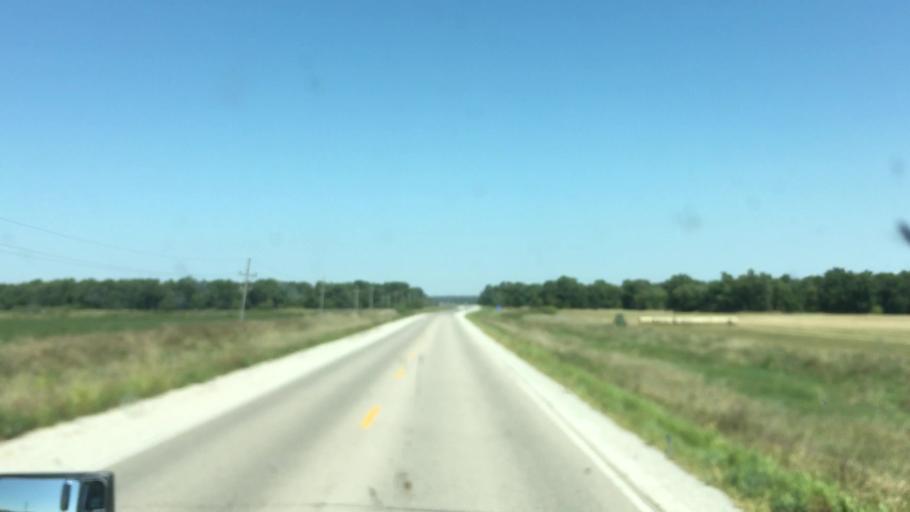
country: US
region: Iowa
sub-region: Benton County
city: Belle Plaine
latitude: 41.8525
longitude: -92.2783
